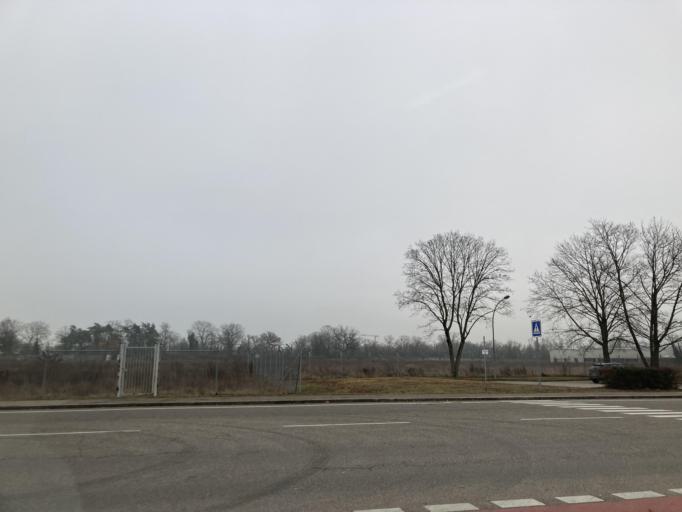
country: DE
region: Baden-Wuerttemberg
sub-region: Freiburg Region
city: Neuenburg am Rhein
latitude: 47.8059
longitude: 7.5516
